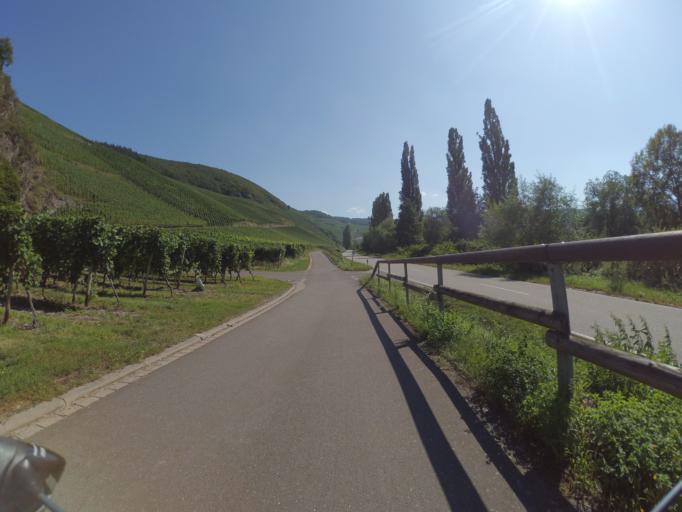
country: DE
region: Rheinland-Pfalz
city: Trittenheim
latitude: 49.8295
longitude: 6.9039
